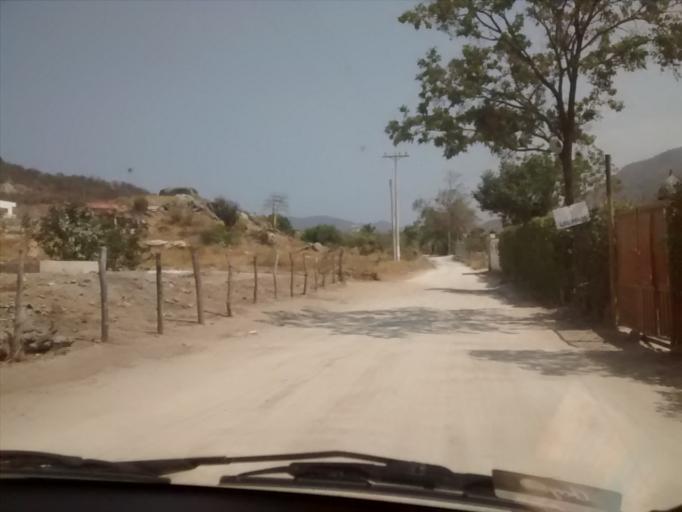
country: CO
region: Magdalena
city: Santa Marta
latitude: 11.1632
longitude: -74.2194
